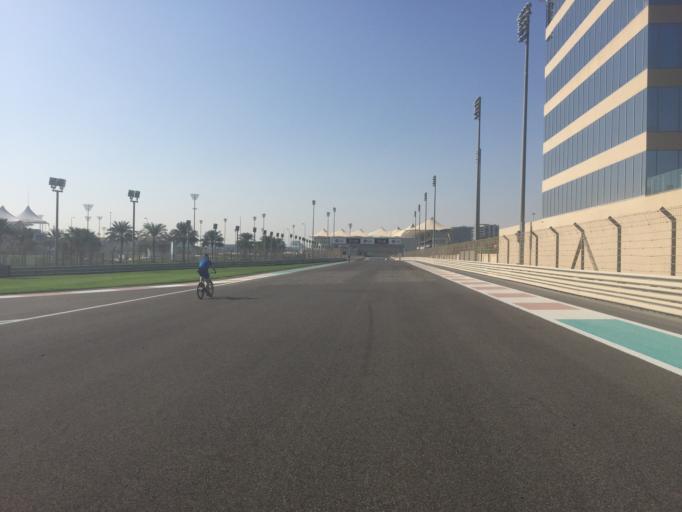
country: AE
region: Abu Dhabi
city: Abu Dhabi
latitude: 24.4733
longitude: 54.6032
